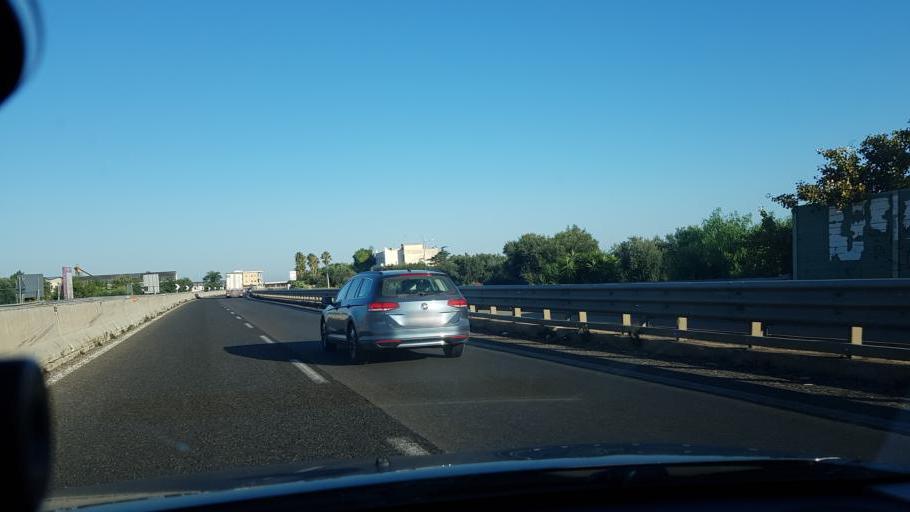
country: IT
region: Apulia
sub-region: Provincia di Brindisi
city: Fasano
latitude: 40.8559
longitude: 17.3522
